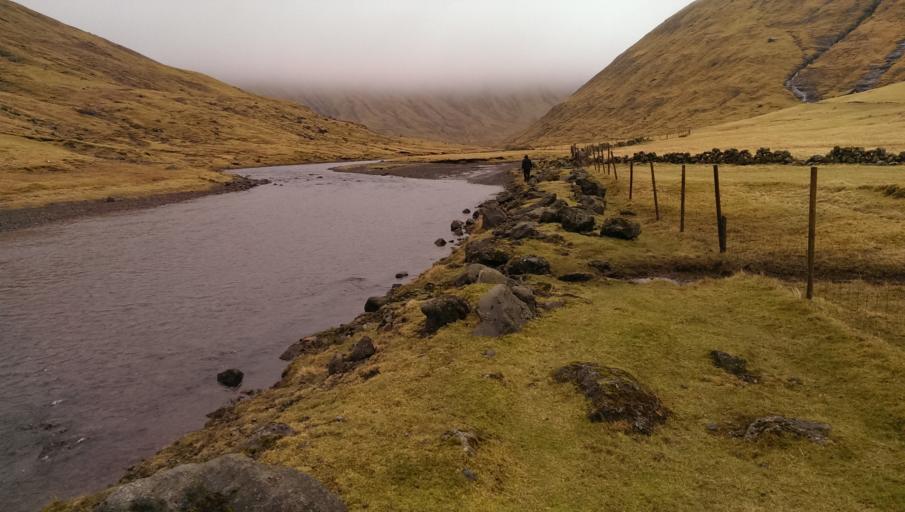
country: FO
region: Streymoy
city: Kollafjordhur
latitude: 62.1338
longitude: -7.0231
